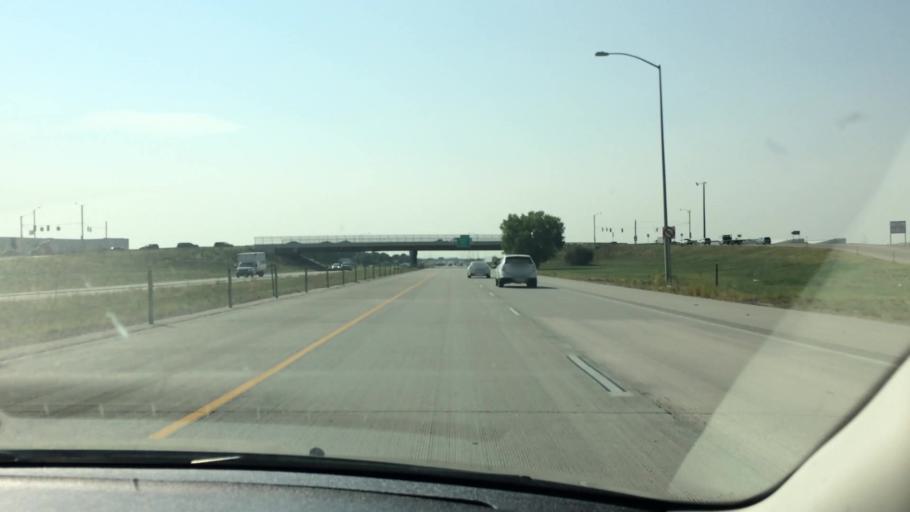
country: US
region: Colorado
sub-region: Adams County
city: Aurora
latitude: 39.7584
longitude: -104.7695
